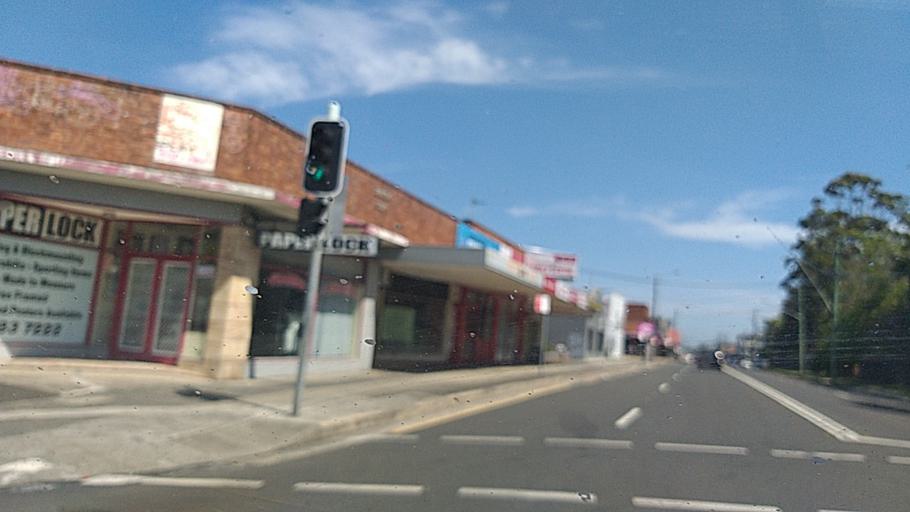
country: AU
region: New South Wales
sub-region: Wollongong
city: Fairy Meadow
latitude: -34.3899
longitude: 150.8937
